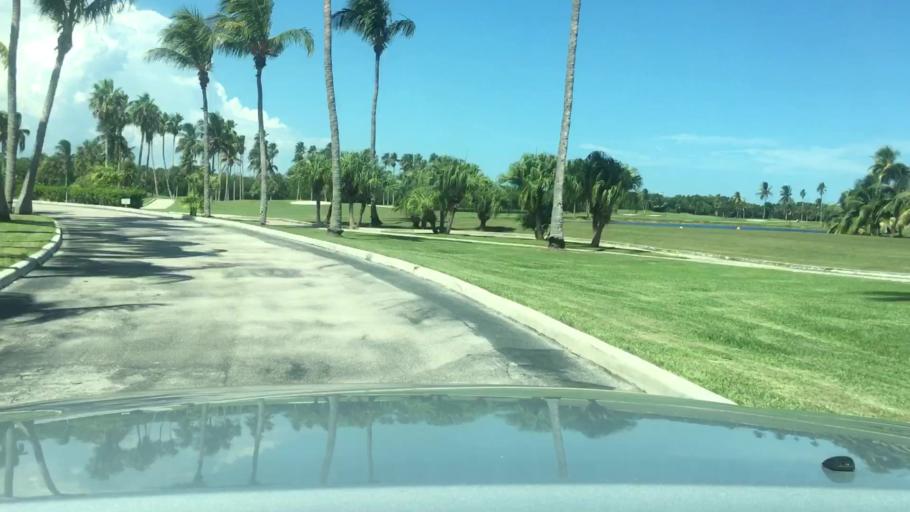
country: US
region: Florida
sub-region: Miami-Dade County
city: Key Biscayne
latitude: 25.7163
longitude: -80.1580
